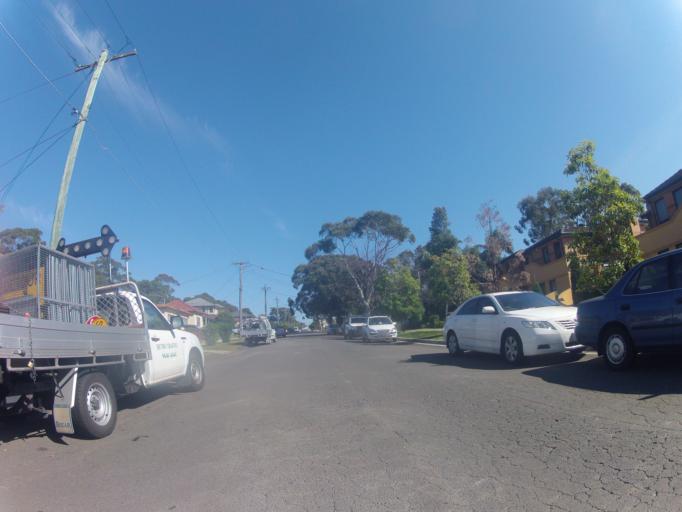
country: AU
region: New South Wales
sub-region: Sutherland Shire
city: Gymea
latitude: -34.0327
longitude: 151.0792
